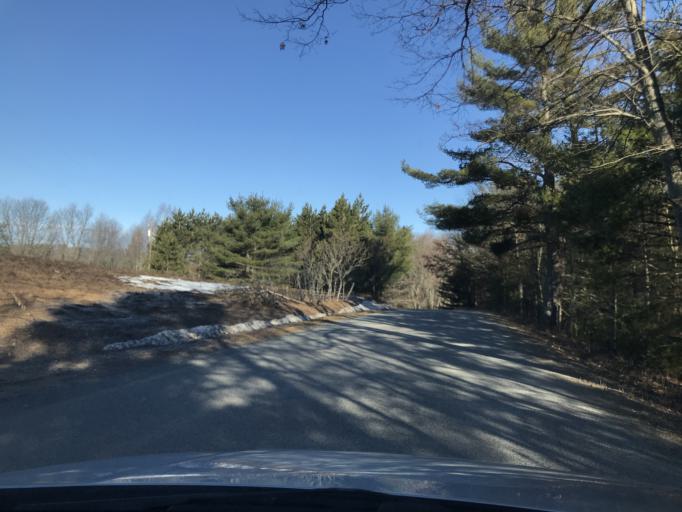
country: US
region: Wisconsin
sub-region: Marinette County
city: Niagara
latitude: 45.3896
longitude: -88.0496
